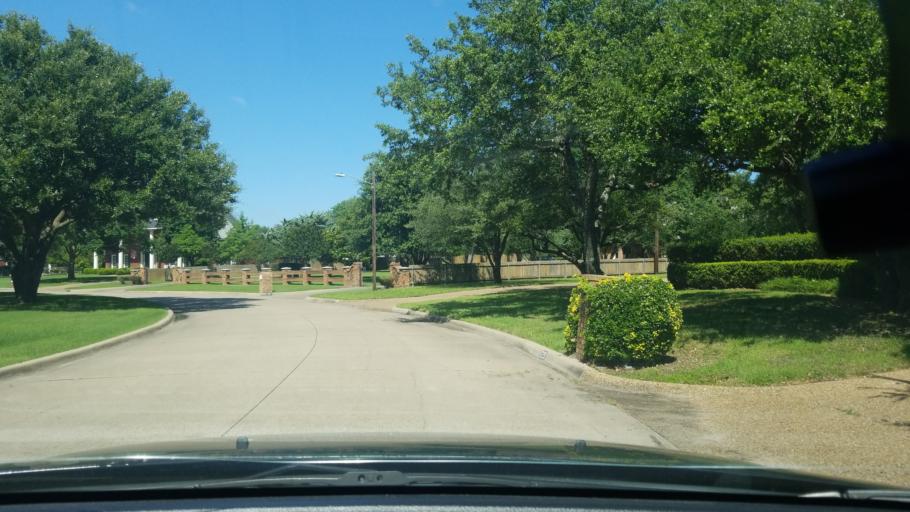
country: US
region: Texas
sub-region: Dallas County
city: Sunnyvale
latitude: 32.8019
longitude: -96.5902
